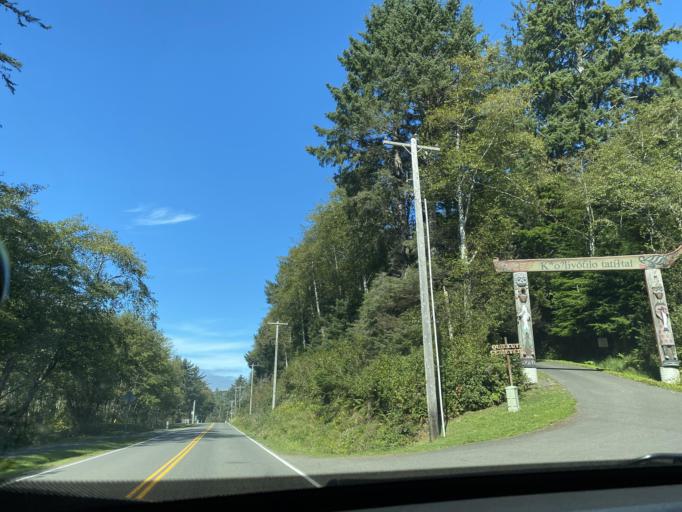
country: US
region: Washington
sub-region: Clallam County
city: Forks
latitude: 47.9024
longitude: -124.6277
